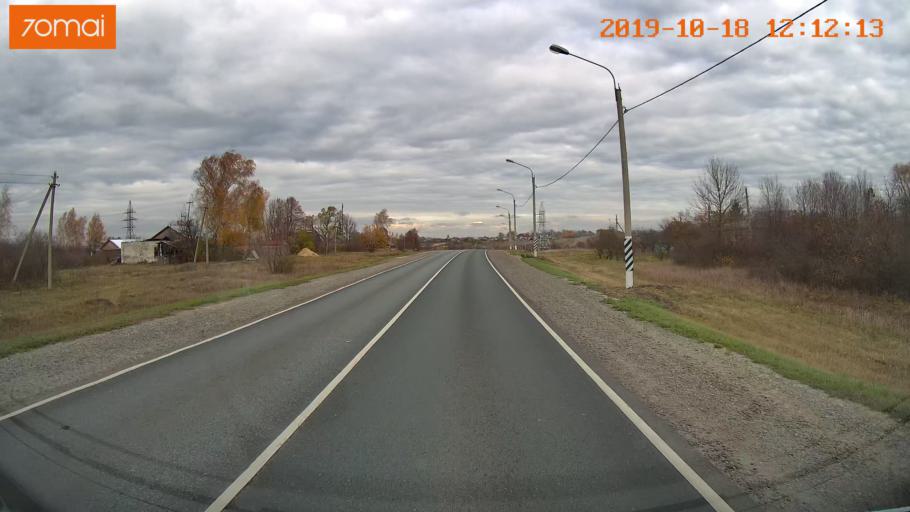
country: RU
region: Rjazan
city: Zakharovo
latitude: 54.4094
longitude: 39.3563
